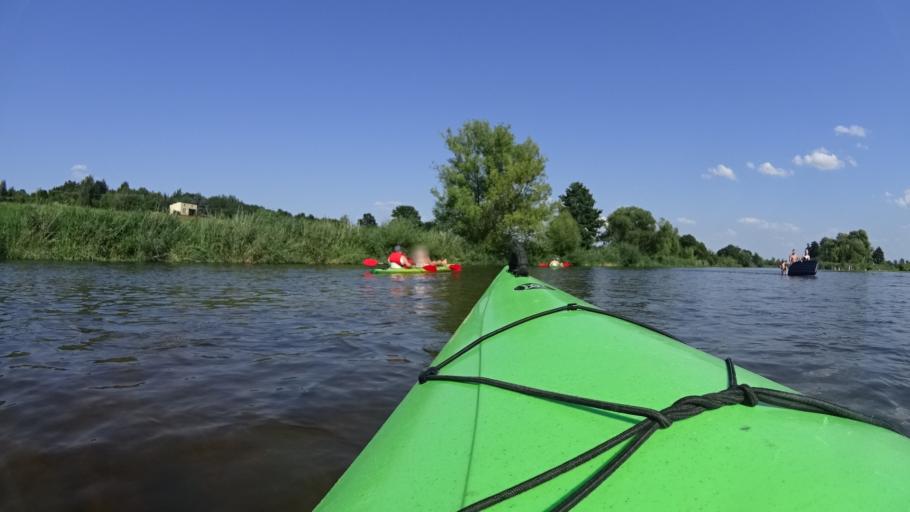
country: PL
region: Masovian Voivodeship
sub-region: Powiat bialobrzeski
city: Bialobrzegi
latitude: 51.6649
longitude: 20.9197
